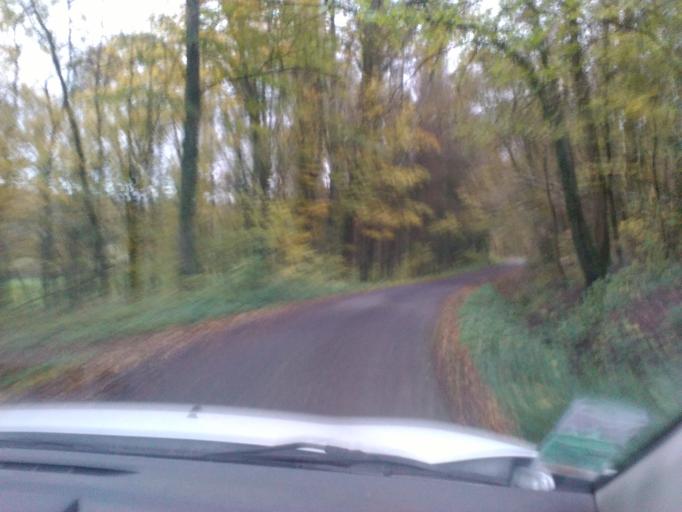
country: FR
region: Lorraine
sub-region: Departement des Vosges
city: Mirecourt
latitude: 48.2795
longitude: 6.2101
